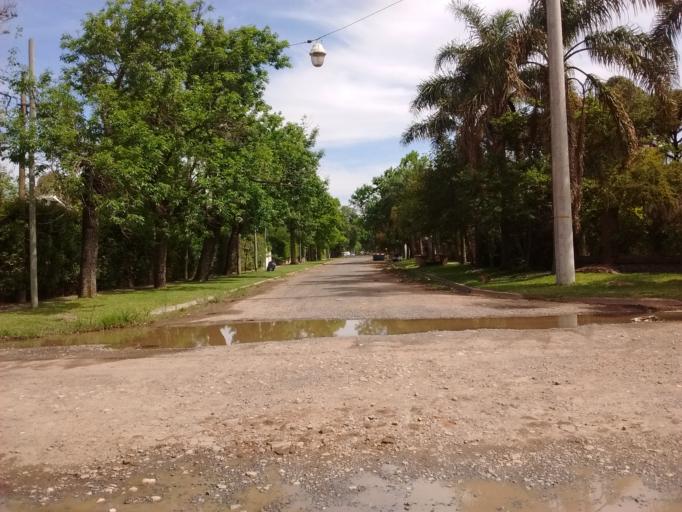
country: AR
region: Santa Fe
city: Funes
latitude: -32.9149
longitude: -60.8029
